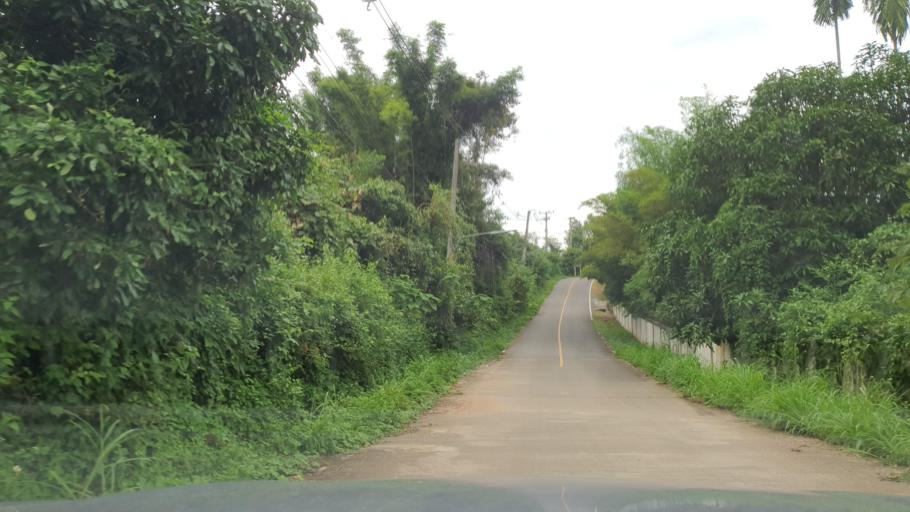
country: TH
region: Chiang Mai
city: Chiang Mai
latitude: 18.9284
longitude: 98.9051
